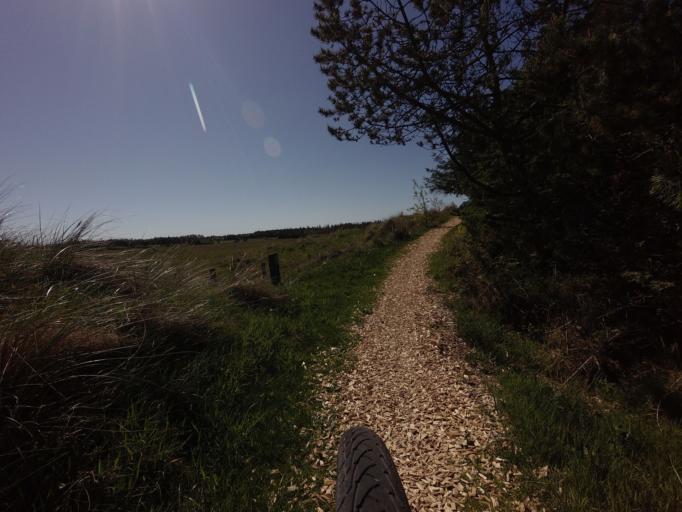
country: DK
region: North Denmark
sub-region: Jammerbugt Kommune
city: Pandrup
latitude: 57.2975
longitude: 9.6450
